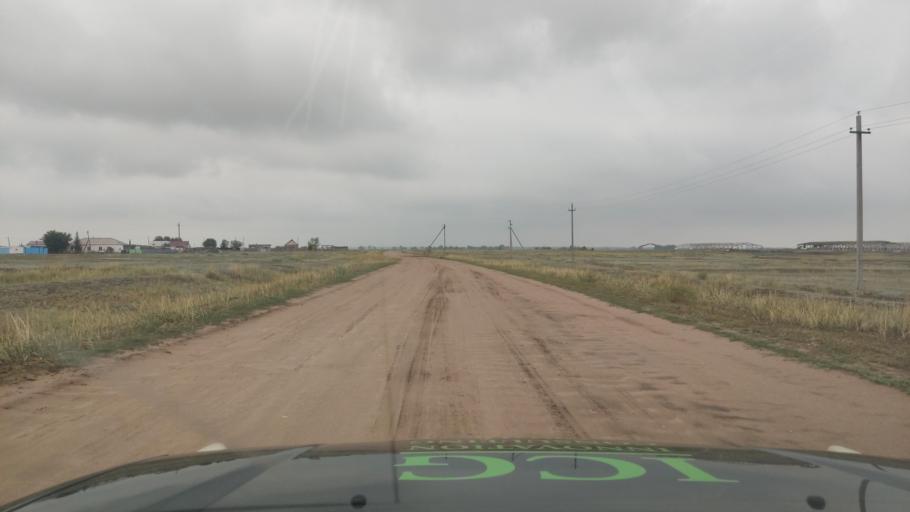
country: KZ
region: Pavlodar
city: Aksu
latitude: 52.0856
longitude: 77.1205
